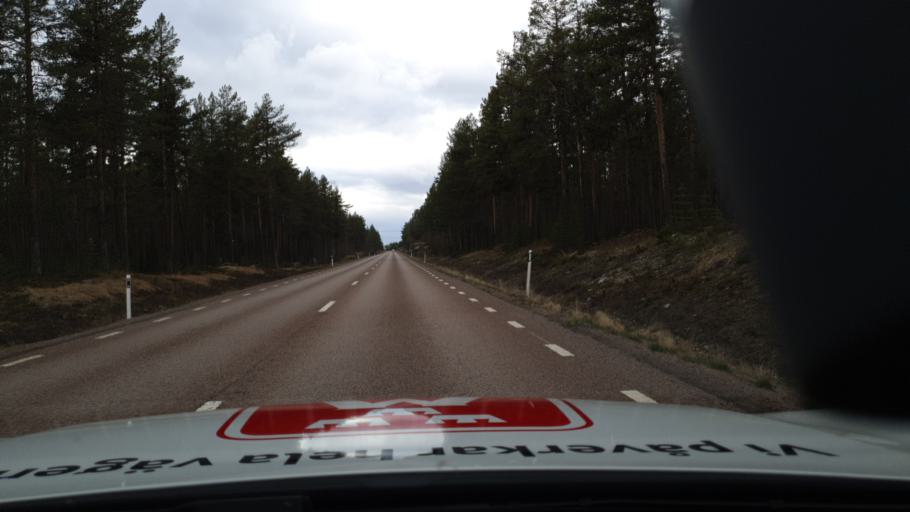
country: SE
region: Jaemtland
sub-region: OEstersunds Kommun
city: Brunflo
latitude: 63.1914
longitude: 15.2473
